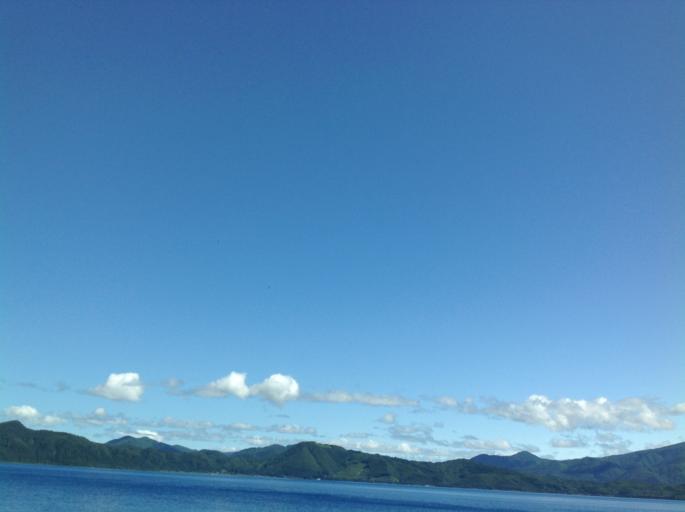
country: JP
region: Akita
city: Kakunodatemachi
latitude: 39.6991
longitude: 140.6587
